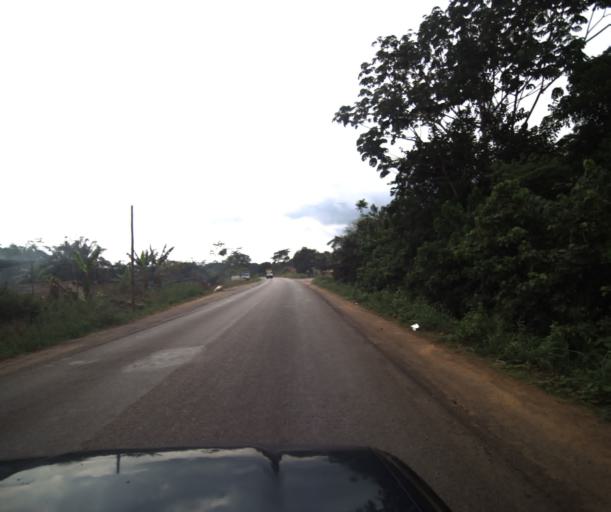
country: CM
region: Littoral
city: Edea
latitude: 3.9498
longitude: 10.0324
